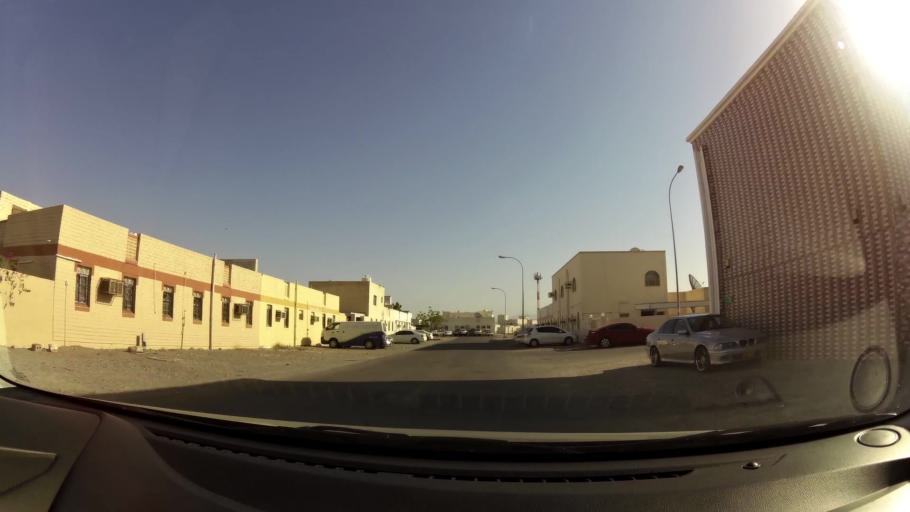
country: OM
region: Muhafazat Masqat
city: As Sib al Jadidah
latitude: 23.6229
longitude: 58.1920
